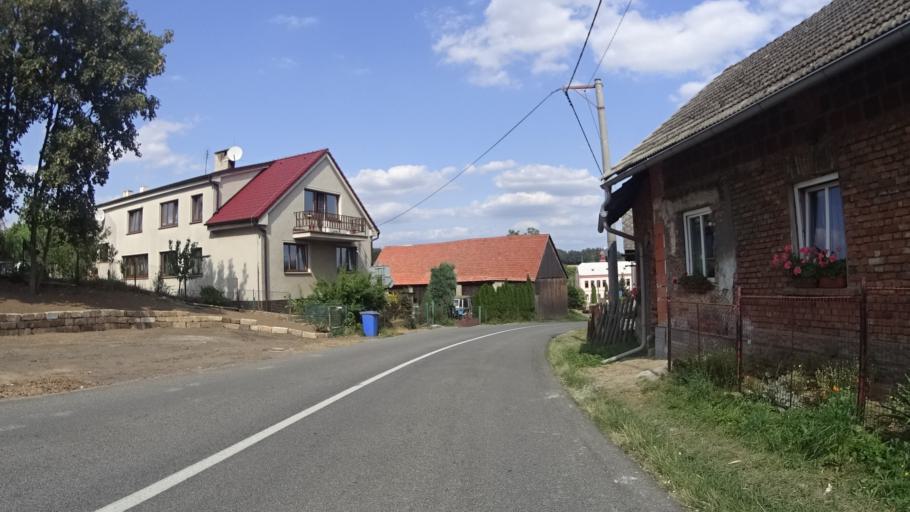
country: CZ
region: Kralovehradecky
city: Liban
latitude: 50.4031
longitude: 15.2729
